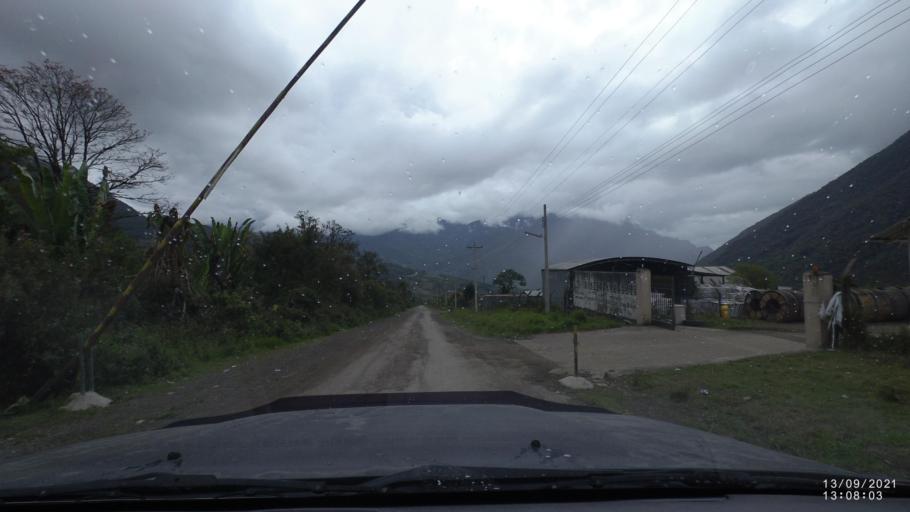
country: BO
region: Cochabamba
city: Colomi
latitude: -17.2181
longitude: -65.8229
